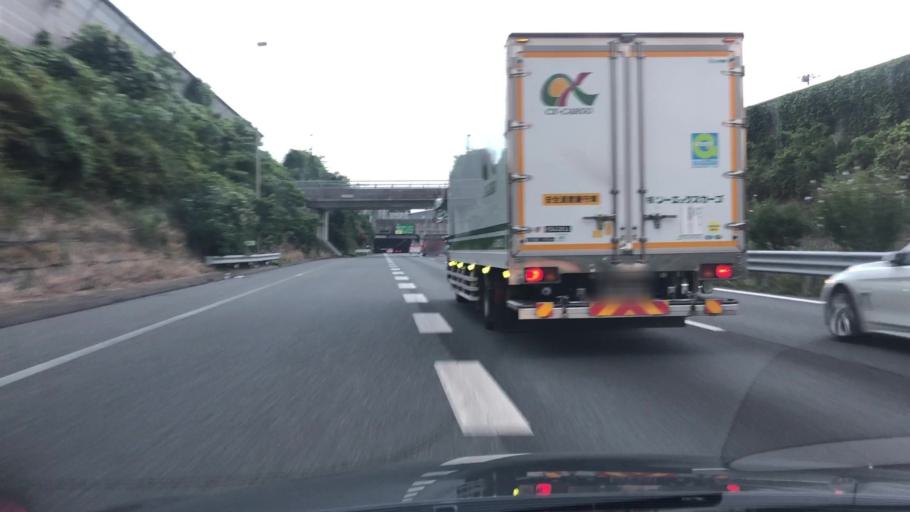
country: JP
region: Tokyo
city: Fussa
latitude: 35.7337
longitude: 139.2828
